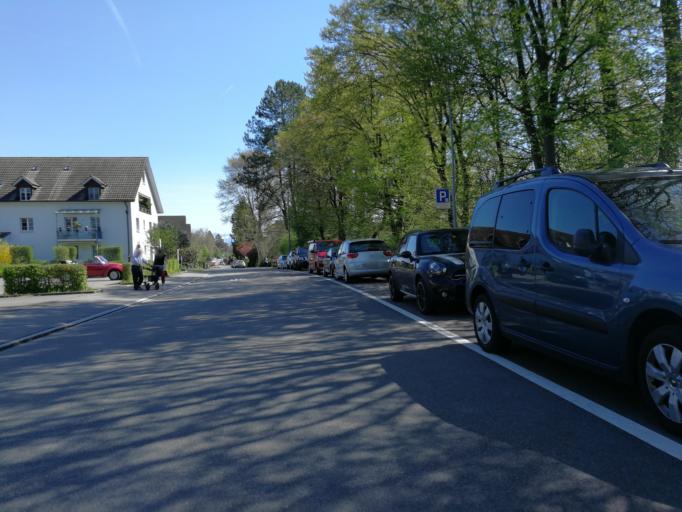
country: CH
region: Zurich
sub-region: Bezirk Meilen
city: Mannedorf
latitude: 47.2560
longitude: 8.6975
